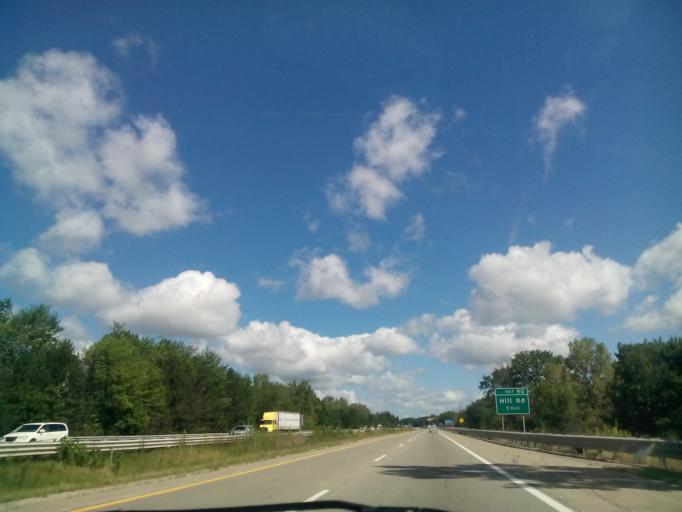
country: US
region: Michigan
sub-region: Genesee County
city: Lake Fenton
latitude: 42.9269
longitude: -83.7249
